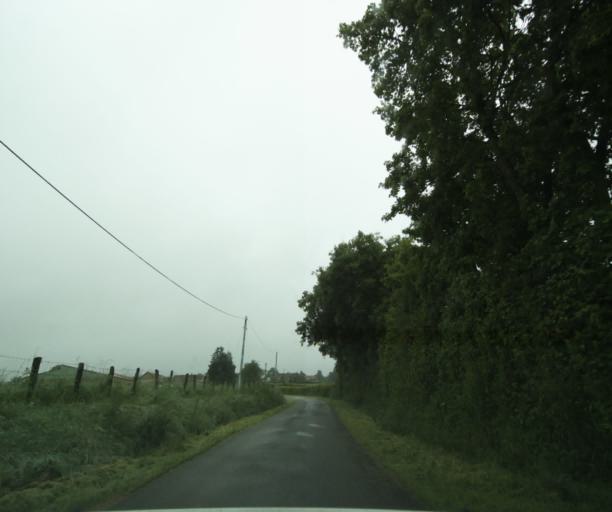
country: FR
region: Bourgogne
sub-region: Departement de Saone-et-Loire
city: Charolles
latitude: 46.3966
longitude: 4.3844
